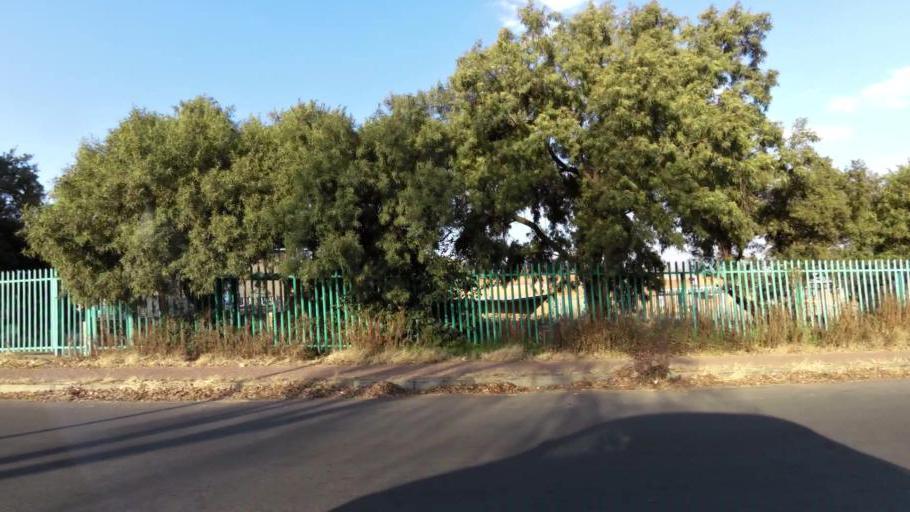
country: ZA
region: Gauteng
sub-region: City of Johannesburg Metropolitan Municipality
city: Soweto
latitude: -26.2201
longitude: 27.8977
